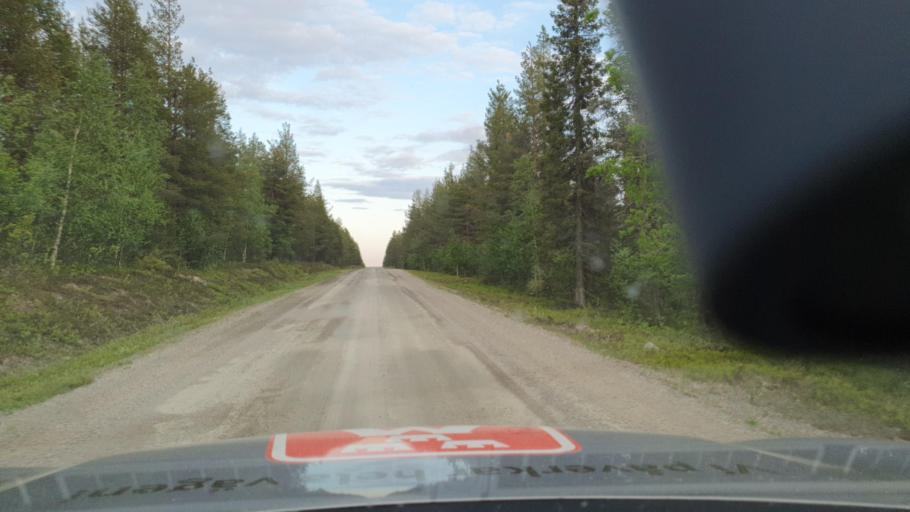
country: SE
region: Norrbotten
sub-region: Gallivare Kommun
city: Gaellivare
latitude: 66.6235
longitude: 21.3418
